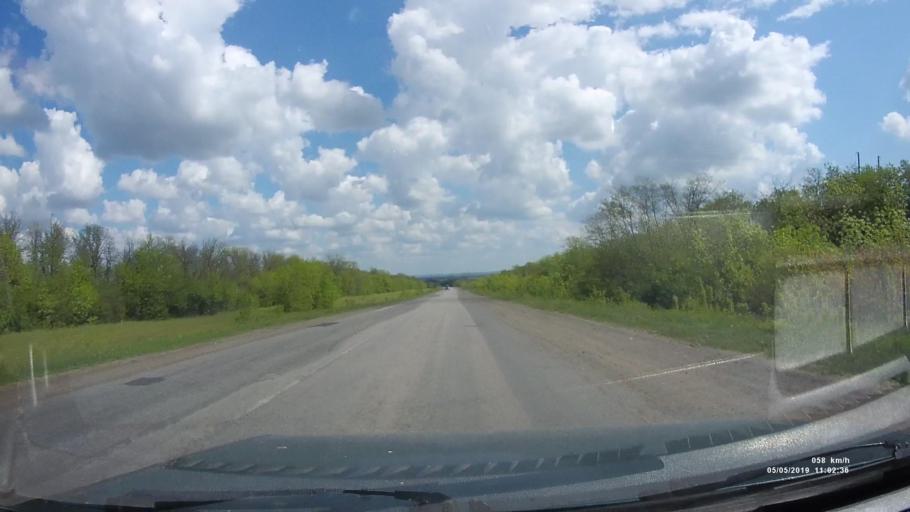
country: RU
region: Rostov
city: Ust'-Donetskiy
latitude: 47.6857
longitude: 40.9102
